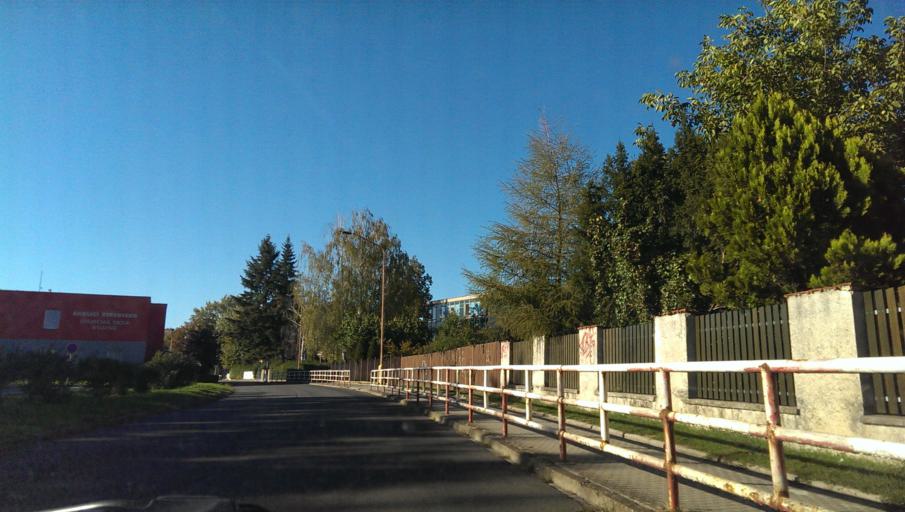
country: CZ
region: Zlin
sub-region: Okres Uherske Hradiste
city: Uherske Hradiste
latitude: 49.0694
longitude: 17.4555
